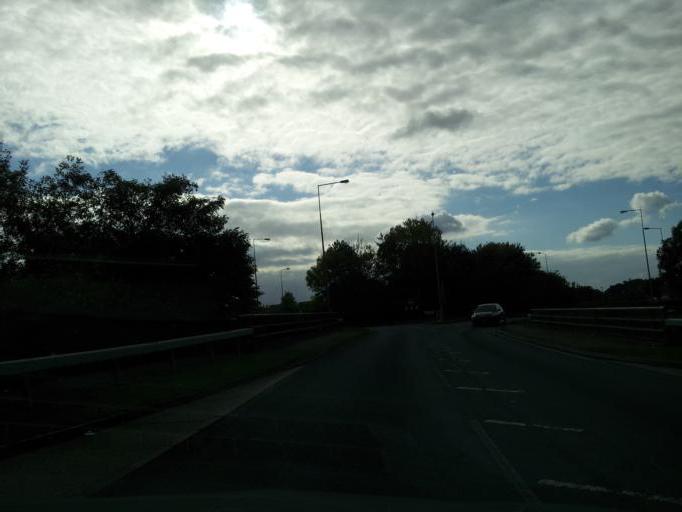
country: GB
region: England
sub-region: Milton Keynes
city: Shenley Church End
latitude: 51.9981
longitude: -0.7972
